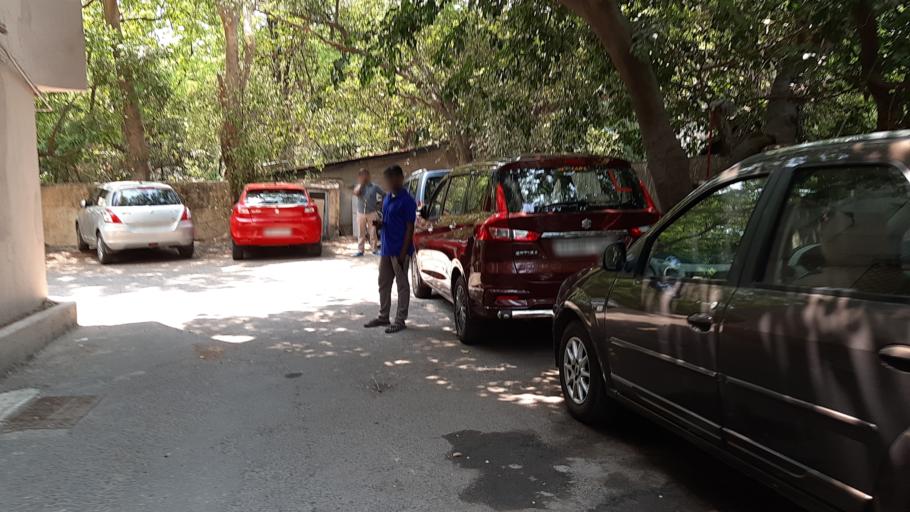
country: IN
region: Tamil Nadu
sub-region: Chennai
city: Chetput
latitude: 13.0474
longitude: 80.2428
